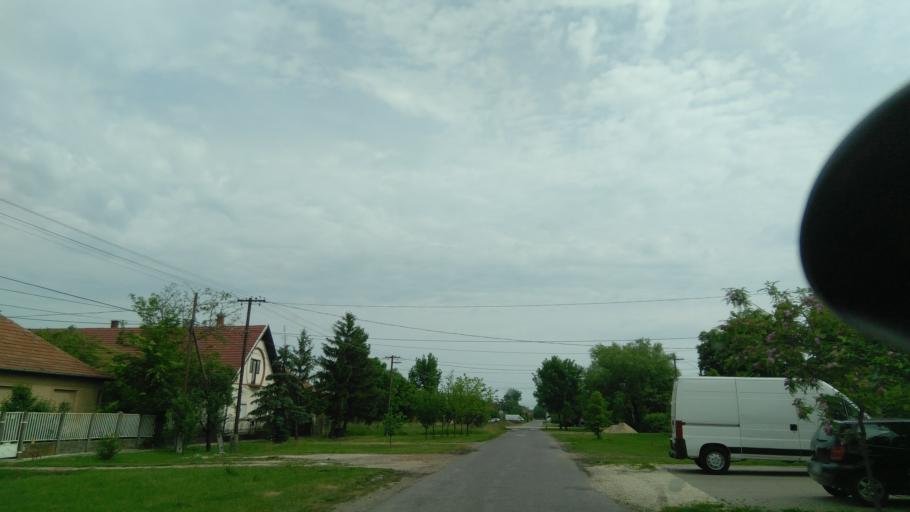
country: HU
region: Bekes
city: Szeghalom
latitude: 47.0199
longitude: 21.1679
